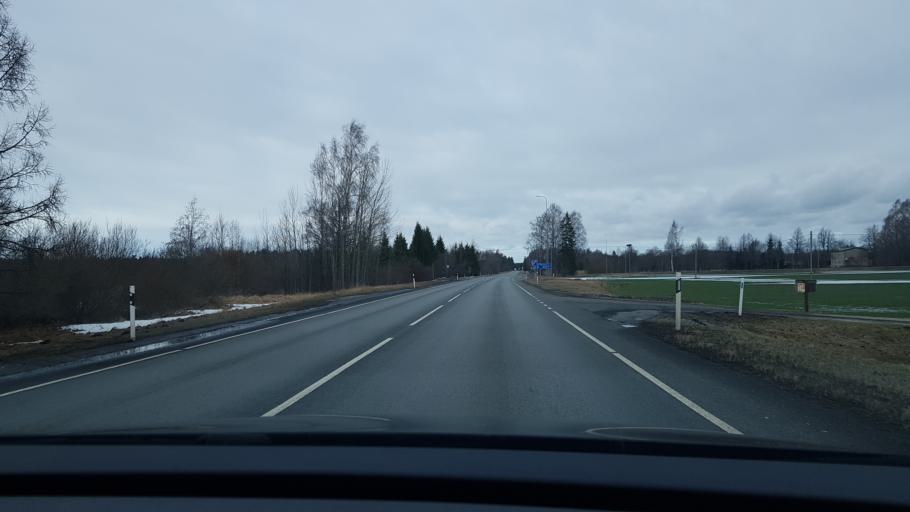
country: EE
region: Paernumaa
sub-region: Paikuse vald
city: Paikuse
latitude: 58.2334
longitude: 24.6969
